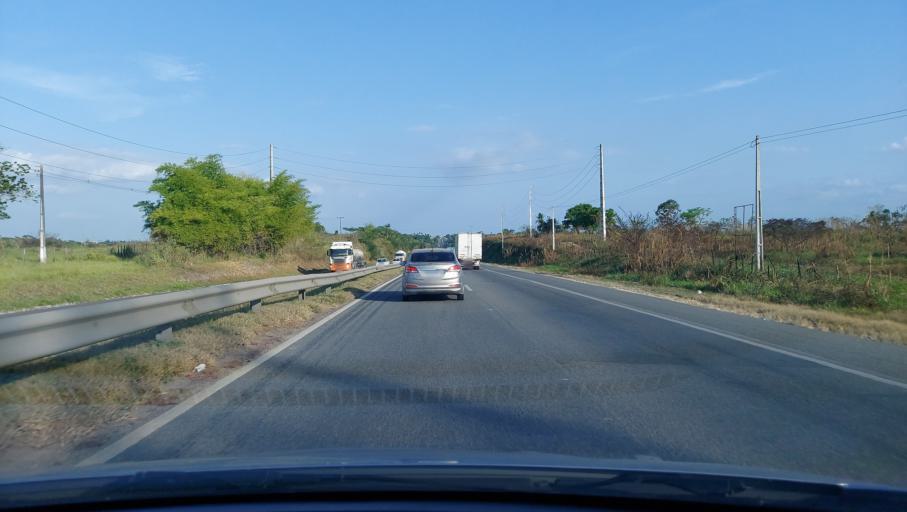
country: BR
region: Bahia
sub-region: Conceicao Do Jacuipe
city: Conceicao do Jacuipe
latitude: -12.3904
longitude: -38.7847
